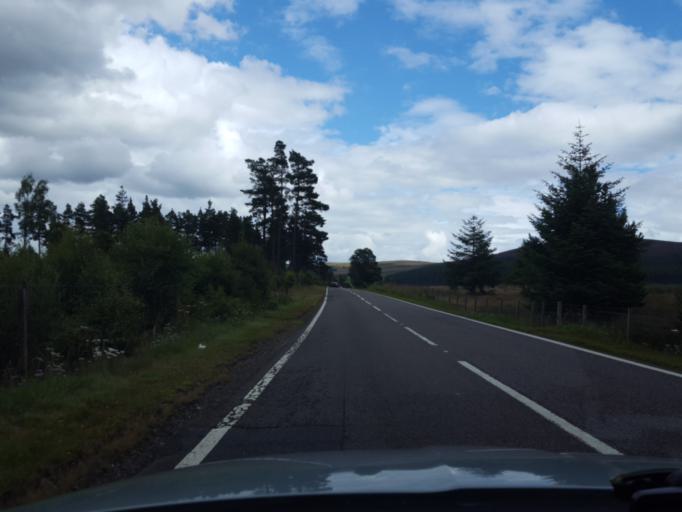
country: GB
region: Scotland
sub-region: Highland
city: Grantown on Spey
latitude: 57.3897
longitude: -3.4500
